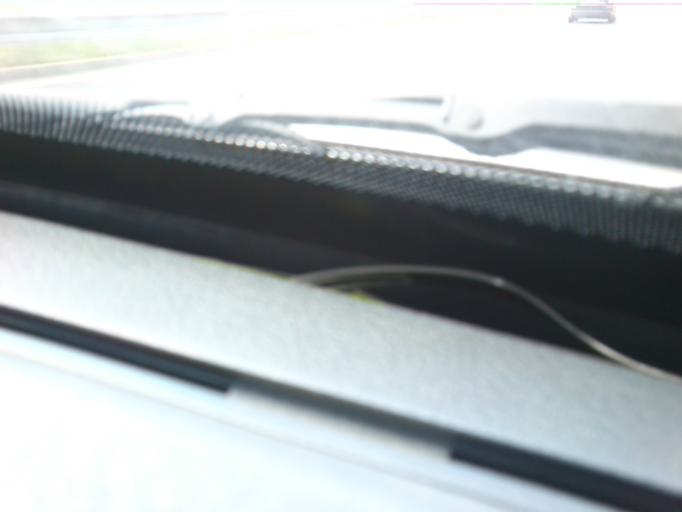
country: CZ
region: Praha
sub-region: Praha 9
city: Strizkov
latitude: 50.1380
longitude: 14.4937
